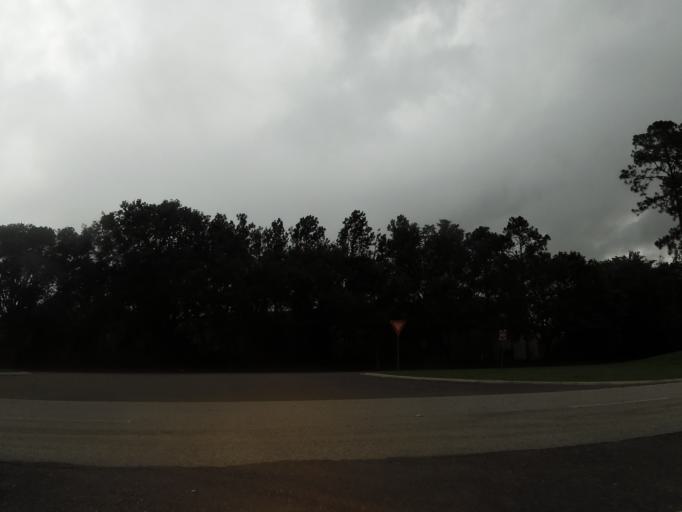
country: US
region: Florida
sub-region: Duval County
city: Neptune Beach
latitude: 30.2825
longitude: -81.5109
